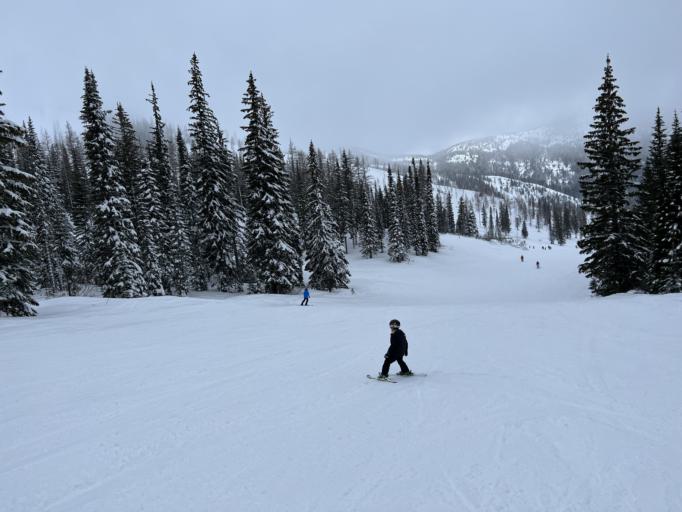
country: US
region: Idaho
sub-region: Bonner County
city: Ponderay
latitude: 48.3817
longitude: -116.6186
